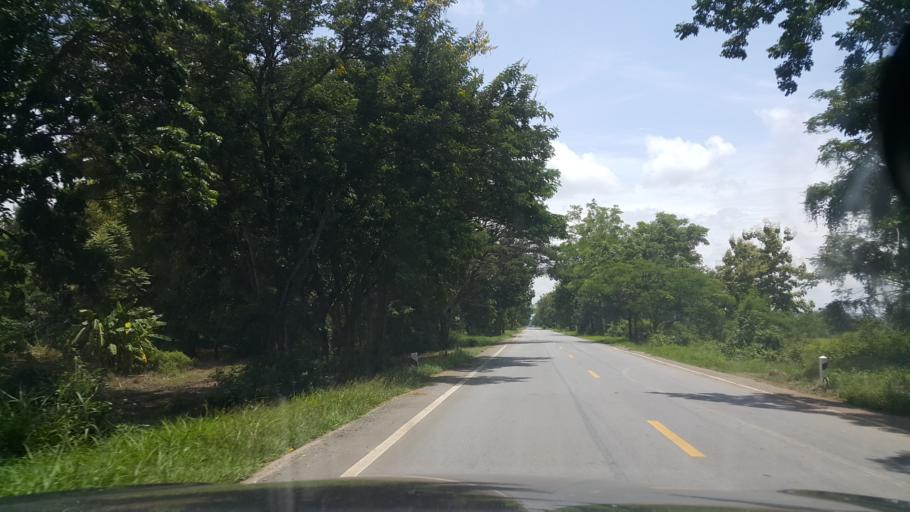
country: TH
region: Sukhothai
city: Sawankhalok
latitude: 17.3344
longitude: 99.7408
